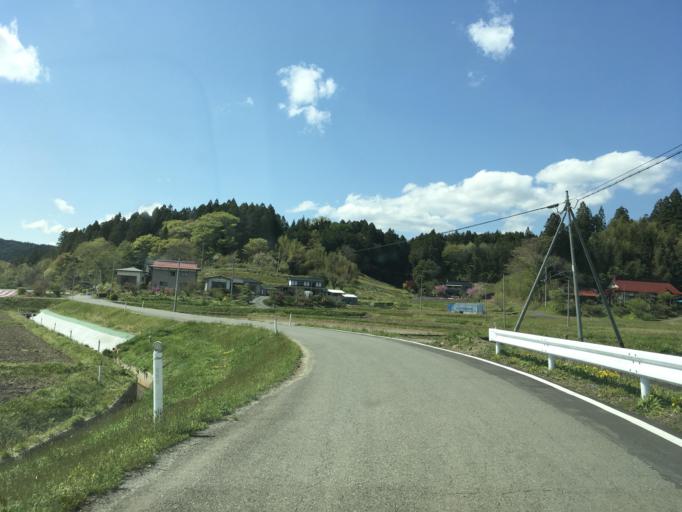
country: JP
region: Iwate
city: Ichinoseki
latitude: 38.8389
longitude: 141.2446
